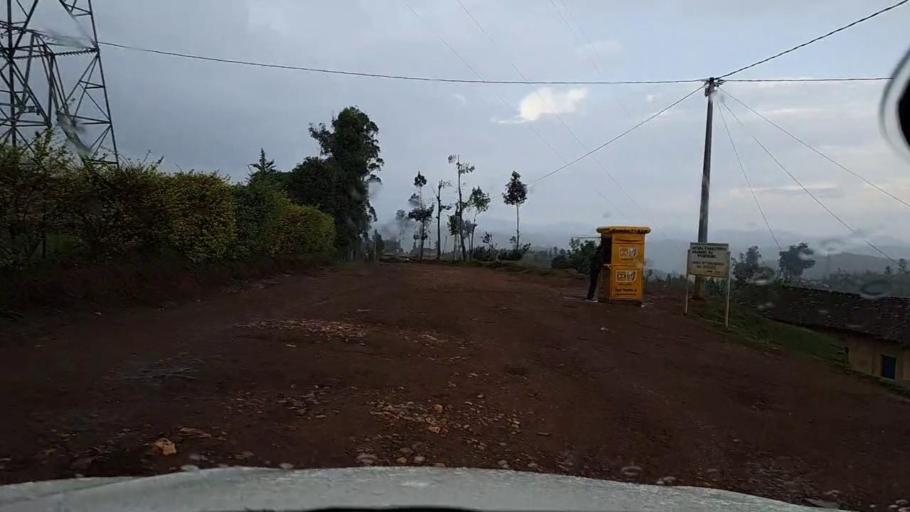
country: BI
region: Kayanza
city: Kayanza
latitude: -2.7802
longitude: 29.5352
